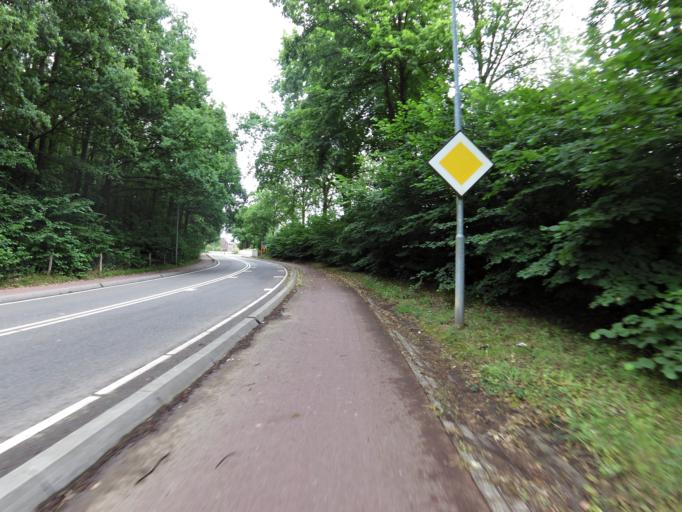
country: NL
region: Limburg
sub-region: Gemeente Voerendaal
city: Klimmen
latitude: 50.8825
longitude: 5.8681
